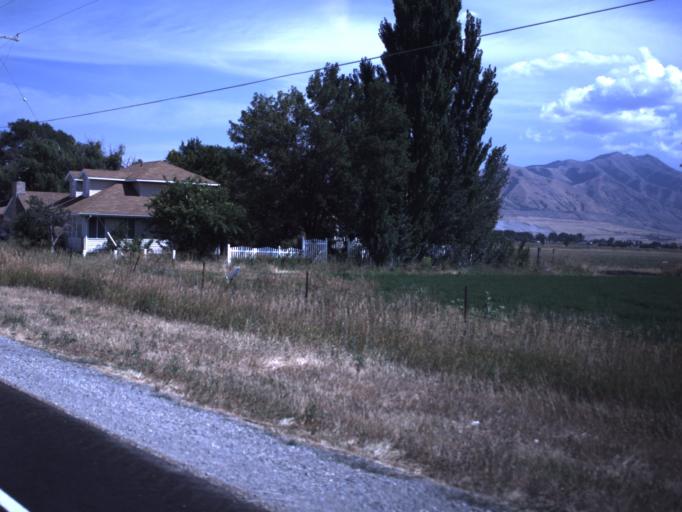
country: US
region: Utah
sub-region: Box Elder County
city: Garland
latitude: 41.7850
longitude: -112.1451
